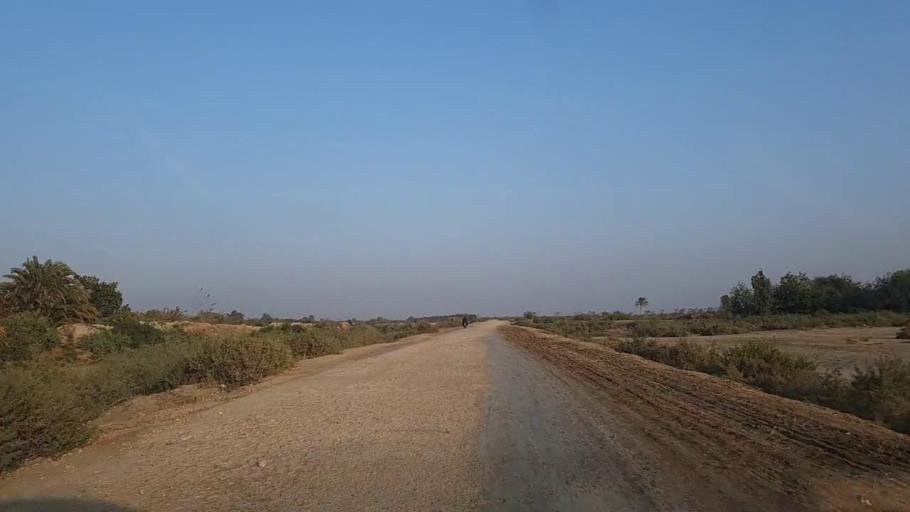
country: PK
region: Sindh
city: Keti Bandar
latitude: 24.2718
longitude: 67.6794
